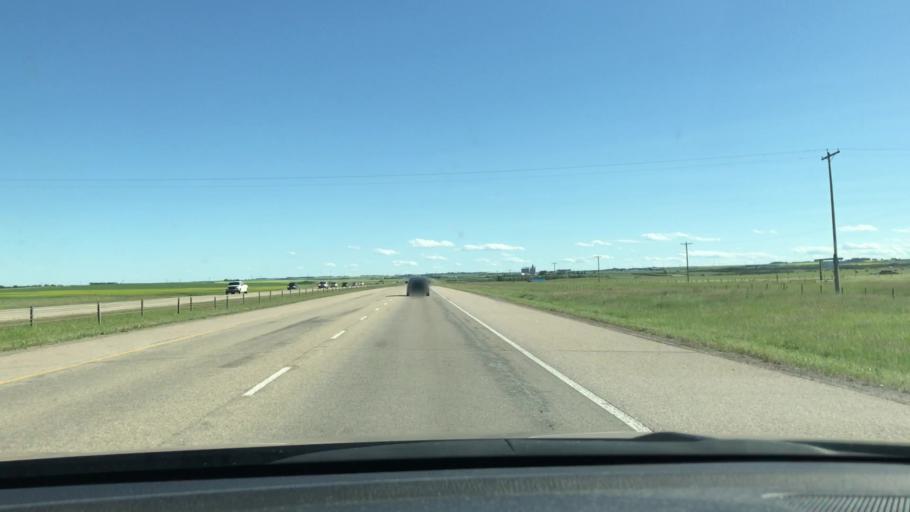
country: CA
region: Alberta
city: Carstairs
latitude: 51.5335
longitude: -114.0254
